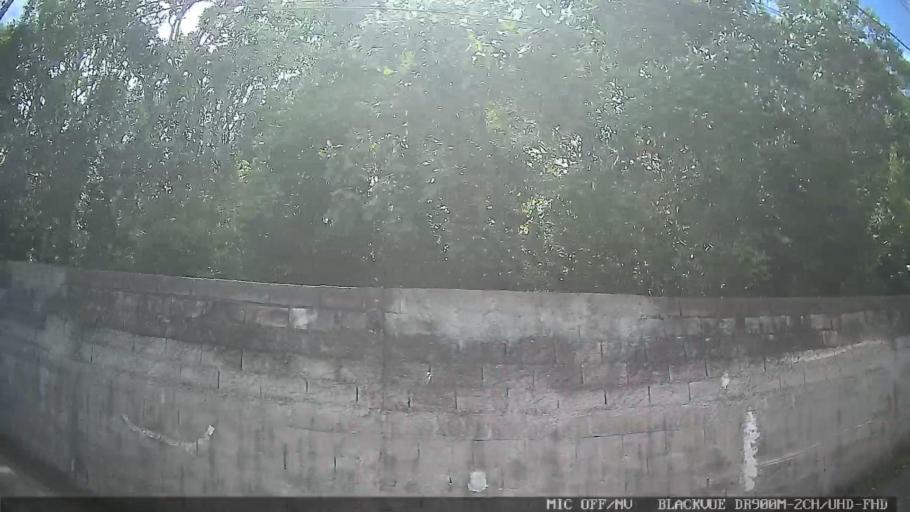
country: BR
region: Sao Paulo
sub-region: Biritiba-Mirim
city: Biritiba Mirim
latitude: -23.5789
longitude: -46.0390
